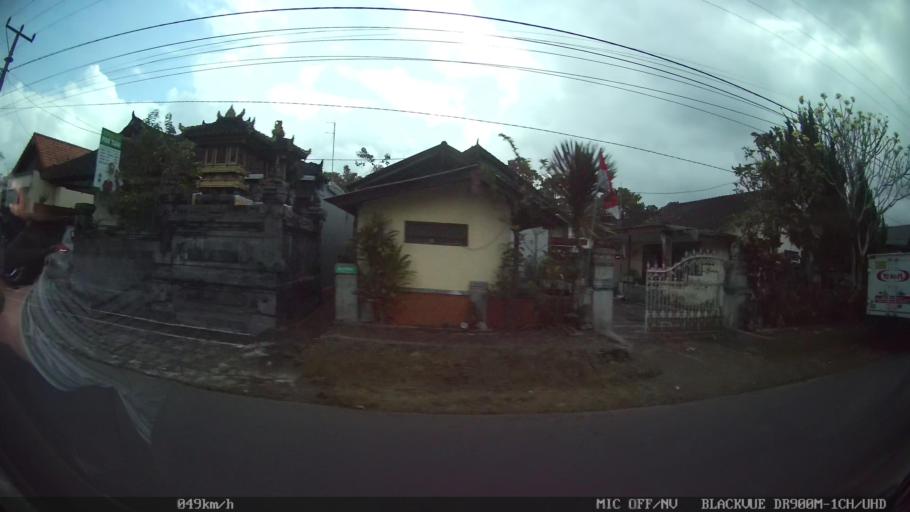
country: ID
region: Bali
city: Pohgending Kawan
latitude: -8.4569
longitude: 115.1385
